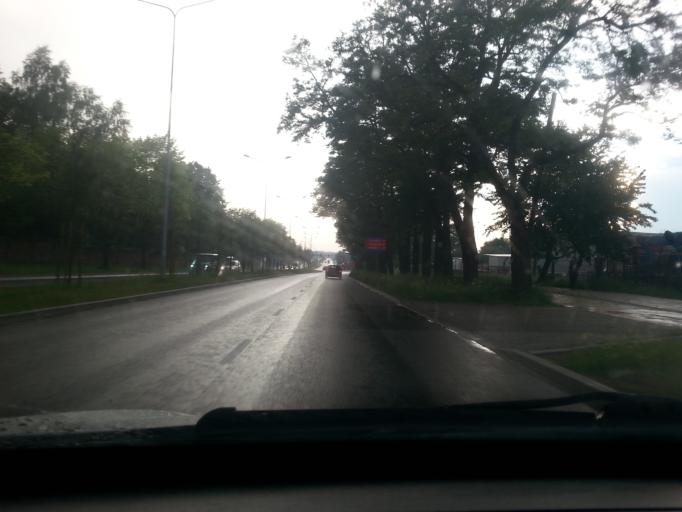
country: PL
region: Lodz Voivodeship
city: Lodz
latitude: 51.8001
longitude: 19.4810
